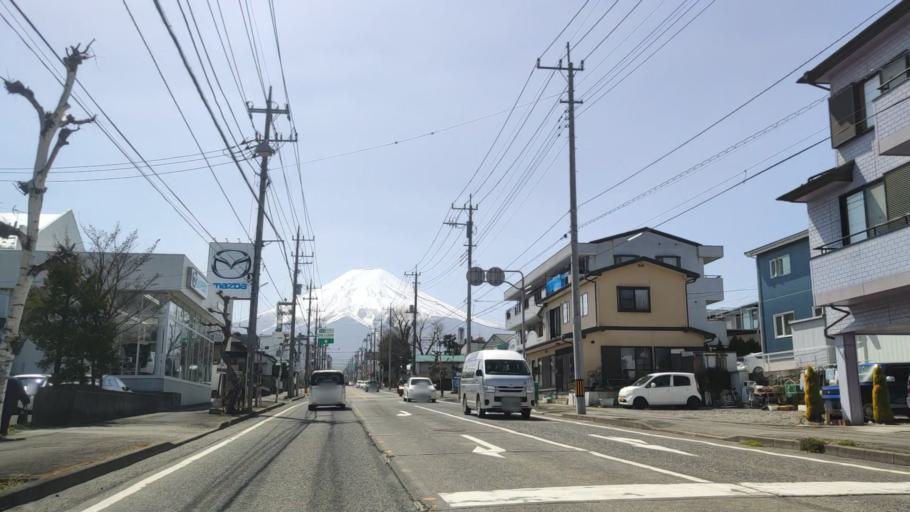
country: JP
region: Yamanashi
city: Fujikawaguchiko
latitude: 35.4898
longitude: 138.8083
